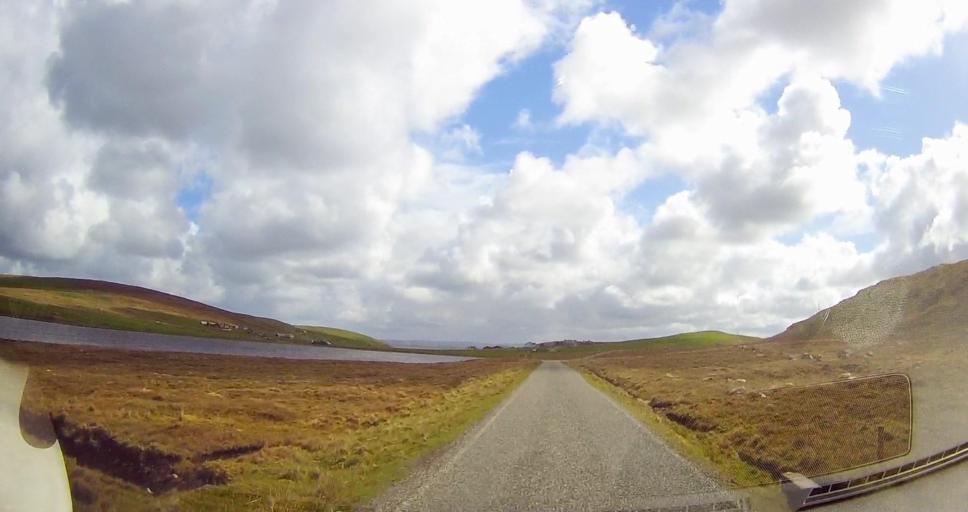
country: GB
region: Scotland
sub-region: Shetland Islands
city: Lerwick
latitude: 60.5506
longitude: -1.3406
